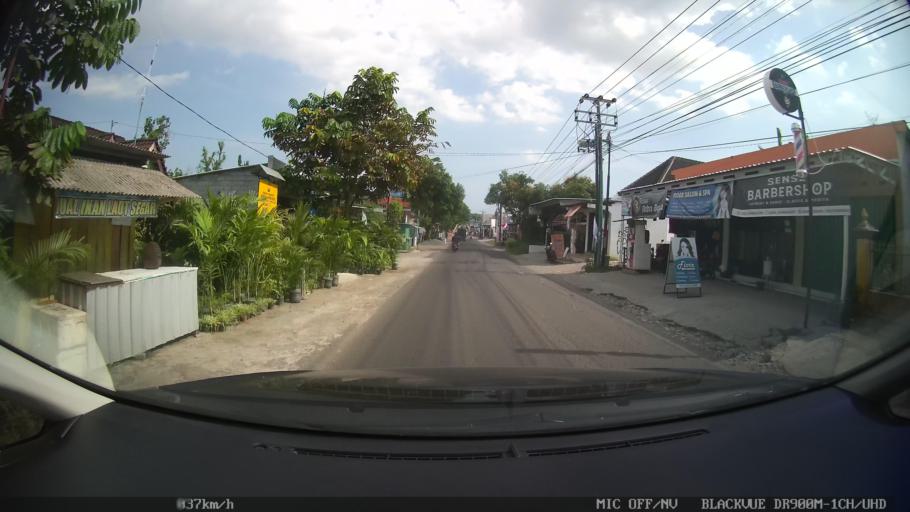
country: ID
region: Daerah Istimewa Yogyakarta
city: Kasihan
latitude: -7.8349
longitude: 110.3131
